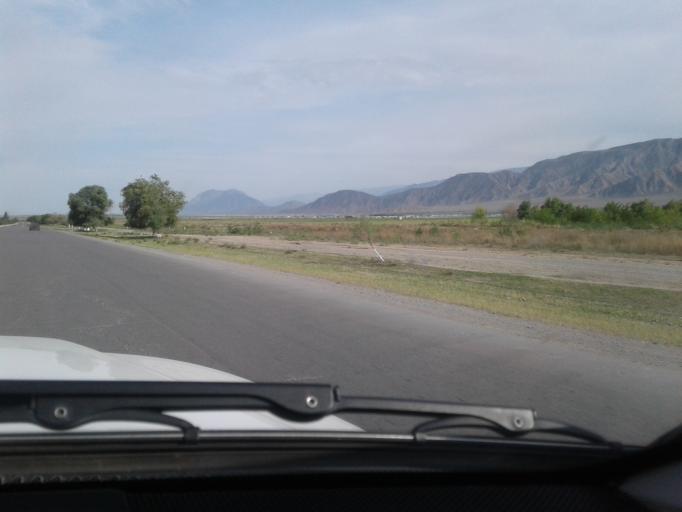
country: TM
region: Ahal
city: Arcabil
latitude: 38.1869
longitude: 57.8515
